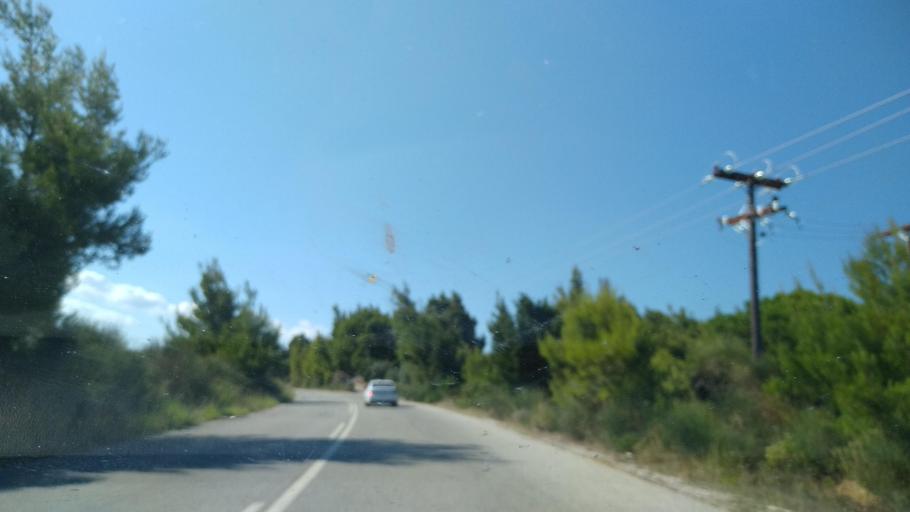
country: GR
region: Central Macedonia
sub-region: Nomos Chalkidikis
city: Agios Nikolaos
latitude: 40.2626
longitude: 23.6968
